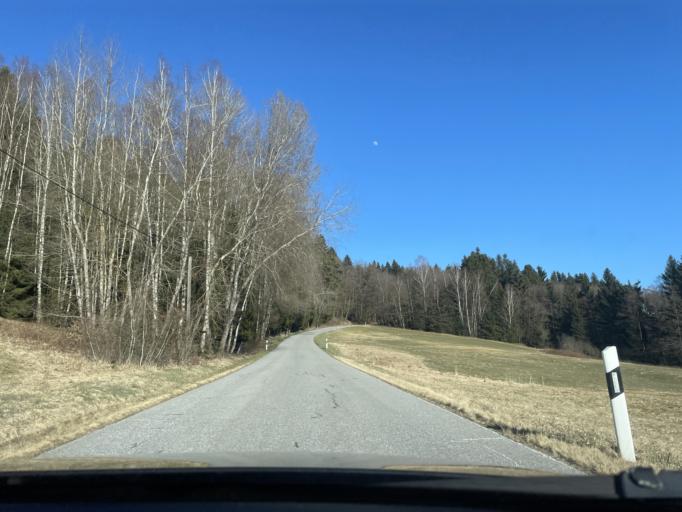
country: DE
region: Bavaria
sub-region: Lower Bavaria
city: Geiersthal
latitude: 49.0805
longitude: 12.9550
